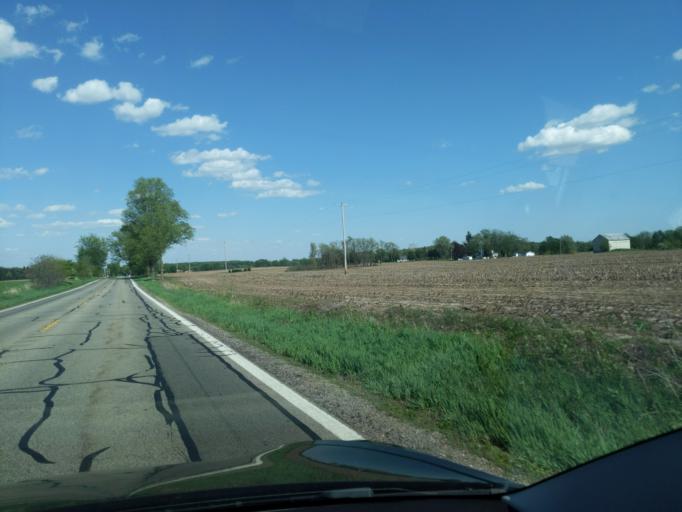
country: US
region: Michigan
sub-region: Kent County
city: Lowell
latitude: 42.7984
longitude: -85.3544
